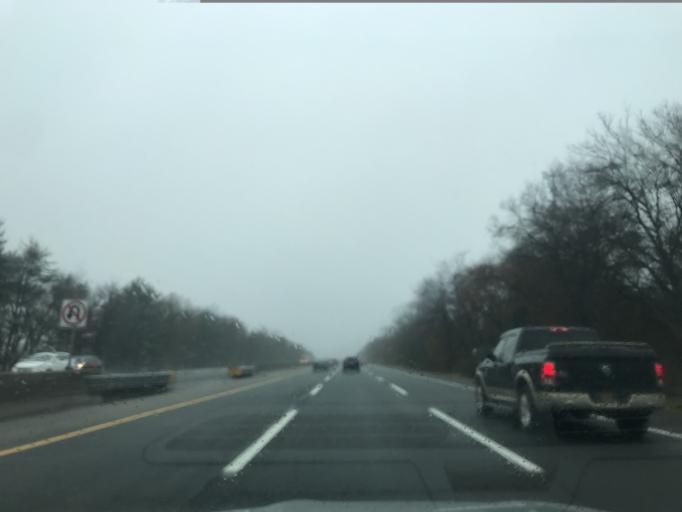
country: US
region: New Jersey
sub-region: Burlington County
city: Willingboro
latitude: 40.0033
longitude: -74.8503
